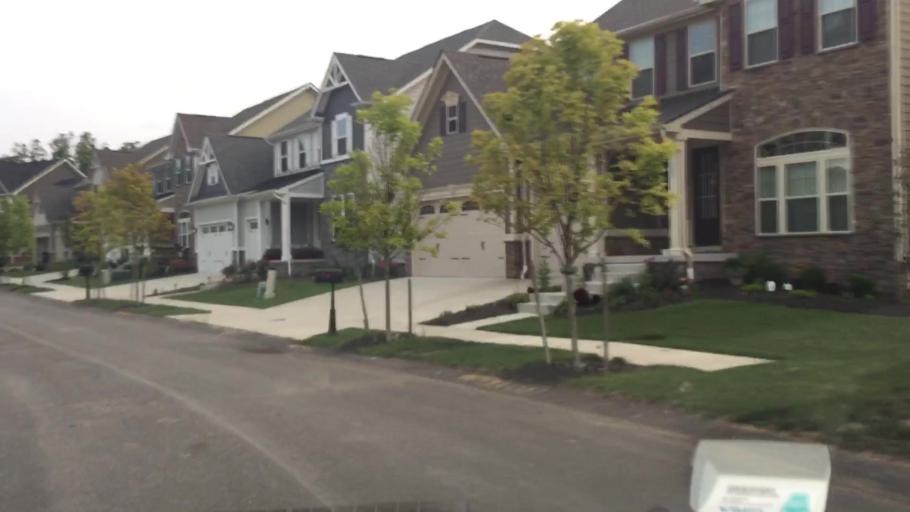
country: US
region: Pennsylvania
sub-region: Allegheny County
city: Bradford Woods
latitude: 40.6611
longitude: -80.0864
